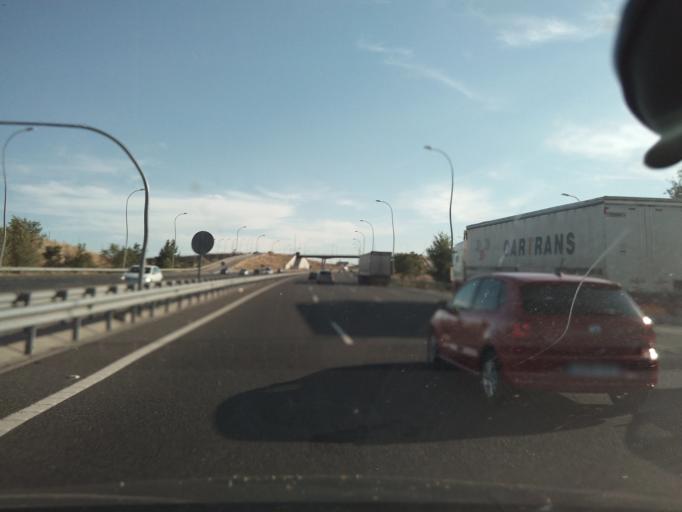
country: ES
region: Madrid
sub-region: Provincia de Madrid
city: Villaverde
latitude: 40.3108
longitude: -3.6509
